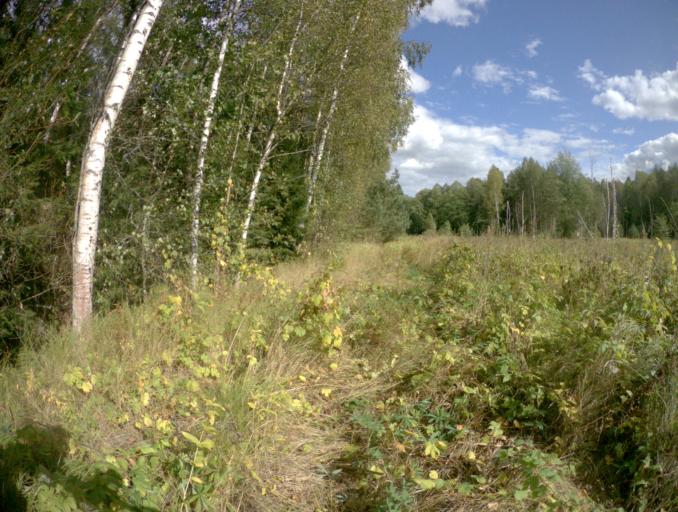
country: RU
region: Vladimir
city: Golovino
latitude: 55.8925
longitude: 40.4356
